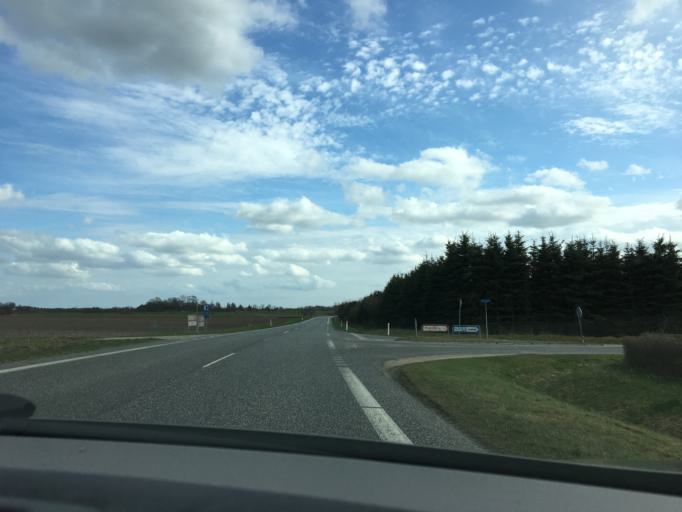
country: DK
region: South Denmark
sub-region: Vejle Kommune
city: Jelling
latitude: 55.7998
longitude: 9.3742
